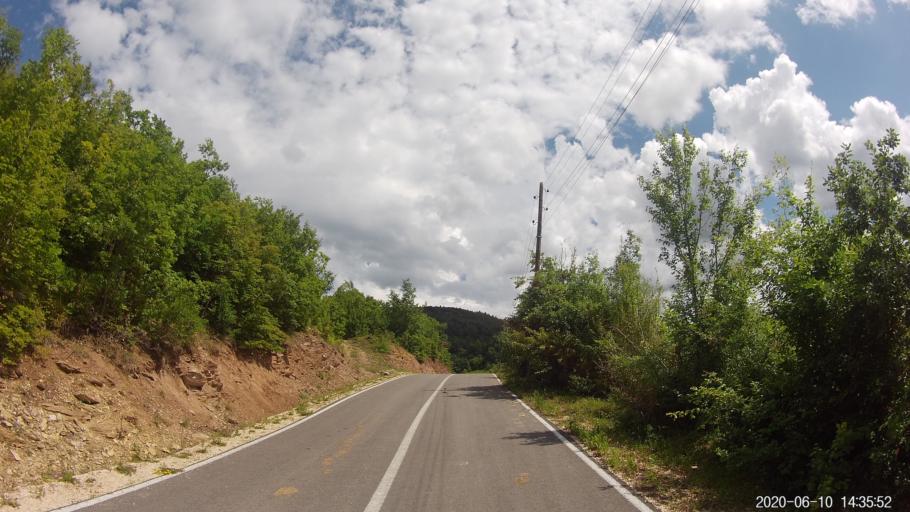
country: XK
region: Prizren
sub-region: Komuna e Therandes
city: Budakovo
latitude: 42.4125
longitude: 20.9354
